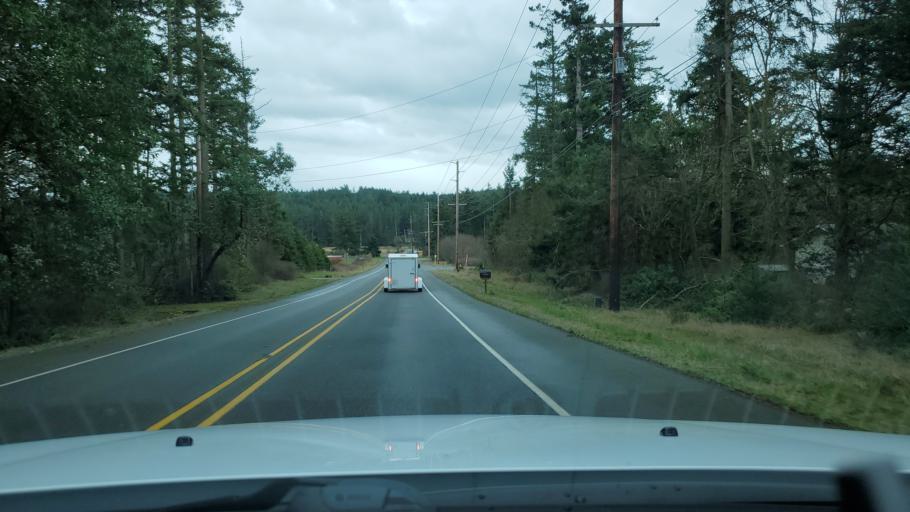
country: US
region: Washington
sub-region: Island County
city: Coupeville
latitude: 48.2350
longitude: -122.7518
